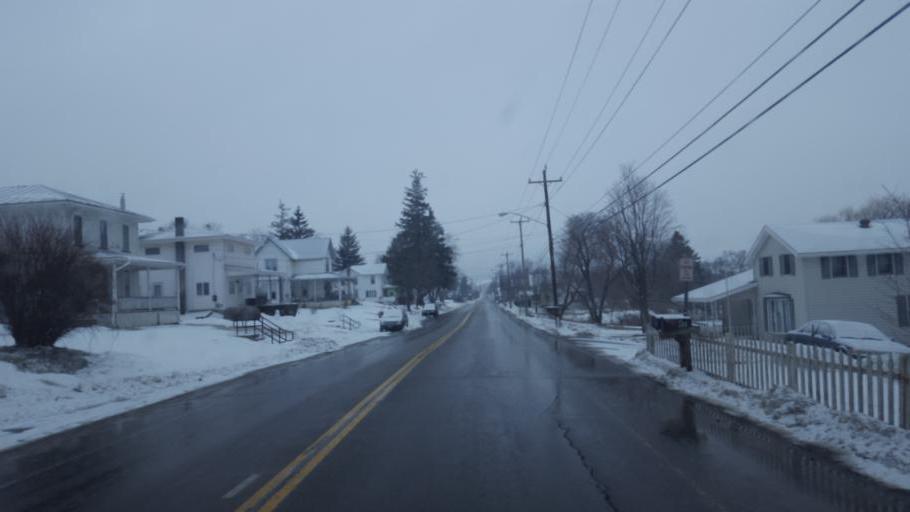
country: US
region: New York
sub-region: Steuben County
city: Canisteo
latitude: 42.1193
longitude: -77.4988
